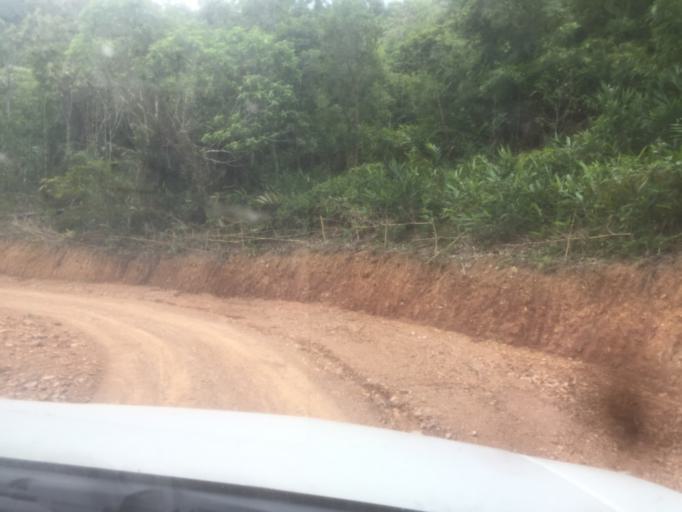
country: LA
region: Phongsali
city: Khoa
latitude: 20.9174
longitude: 102.5612
